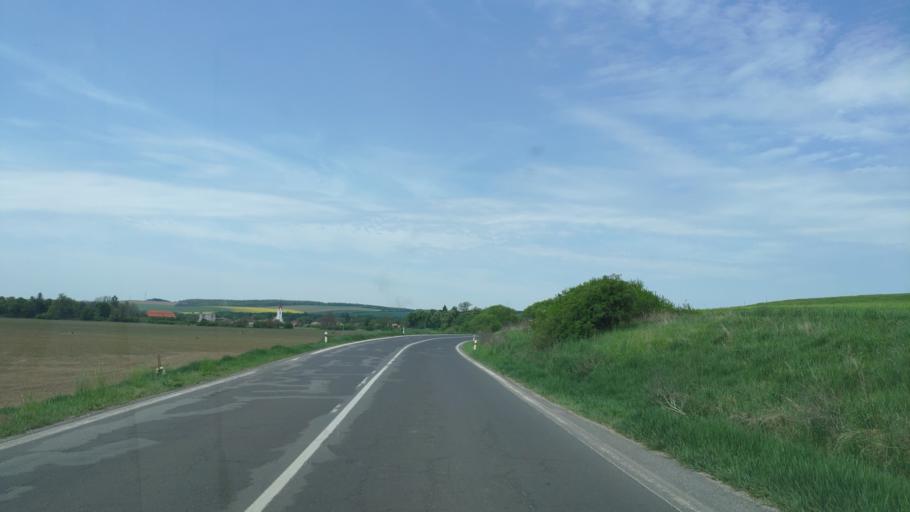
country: HU
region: Borsod-Abauj-Zemplen
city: Putnok
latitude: 48.4271
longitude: 20.3039
